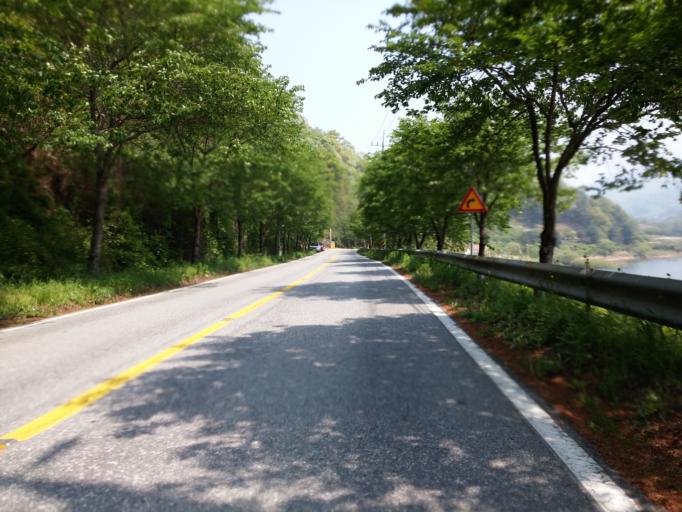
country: KR
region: Chungcheongbuk-do
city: Okcheon
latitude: 36.4350
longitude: 127.5661
